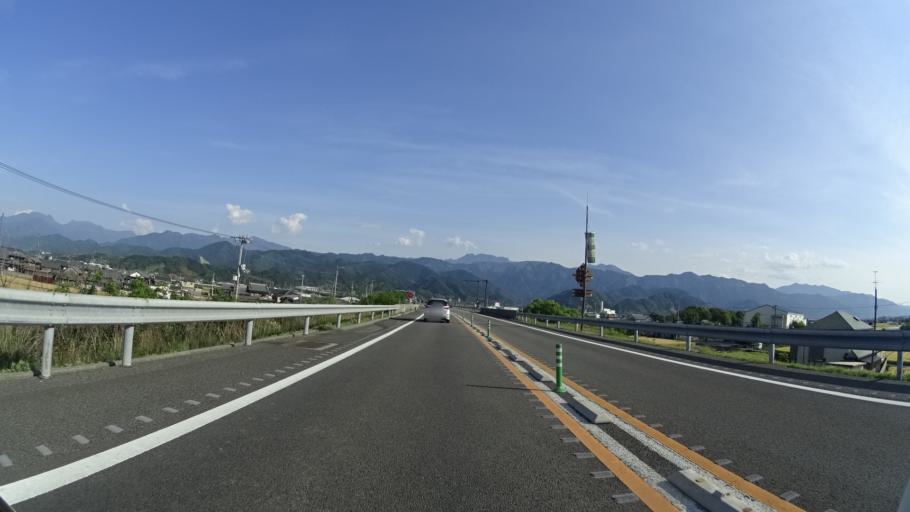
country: JP
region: Ehime
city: Saijo
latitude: 33.9015
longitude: 133.0762
